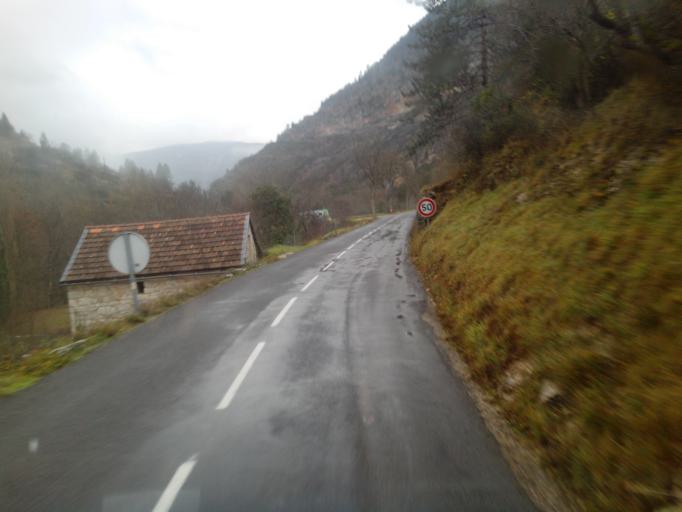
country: FR
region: Languedoc-Roussillon
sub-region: Departement de la Lozere
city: Chanac
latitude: 44.3620
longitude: 3.4112
